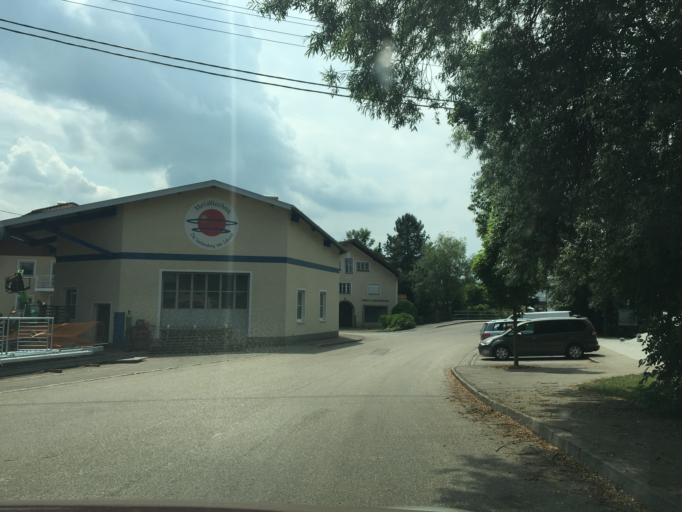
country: AT
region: Upper Austria
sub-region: Politischer Bezirk Braunau am Inn
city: Braunau am Inn
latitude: 48.1900
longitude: 13.1301
